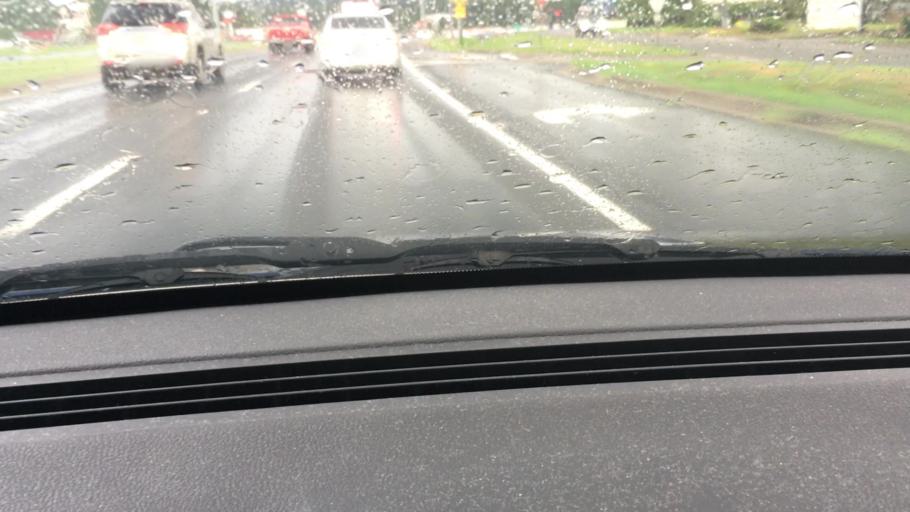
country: US
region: Alabama
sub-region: Tuscaloosa County
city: Tuscaloosa
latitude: 33.2316
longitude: -87.5364
